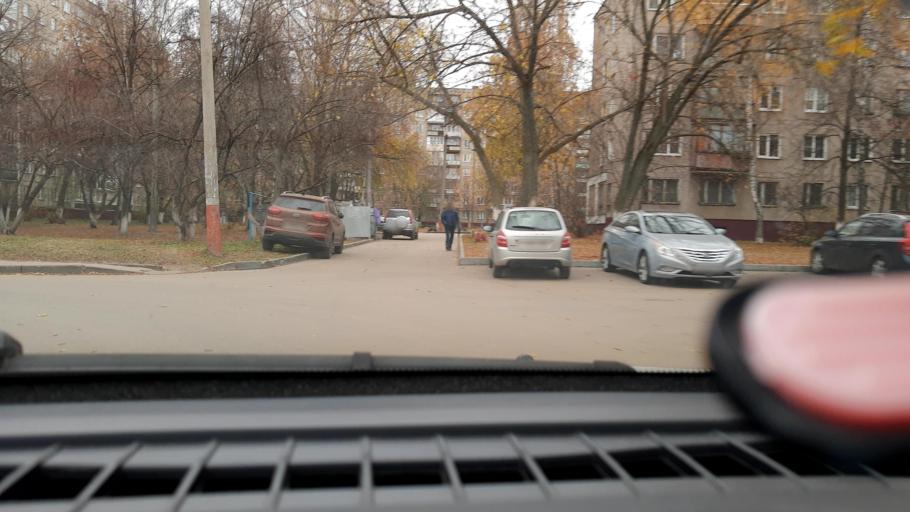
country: RU
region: Nizjnij Novgorod
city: Gorbatovka
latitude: 56.2575
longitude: 43.8817
